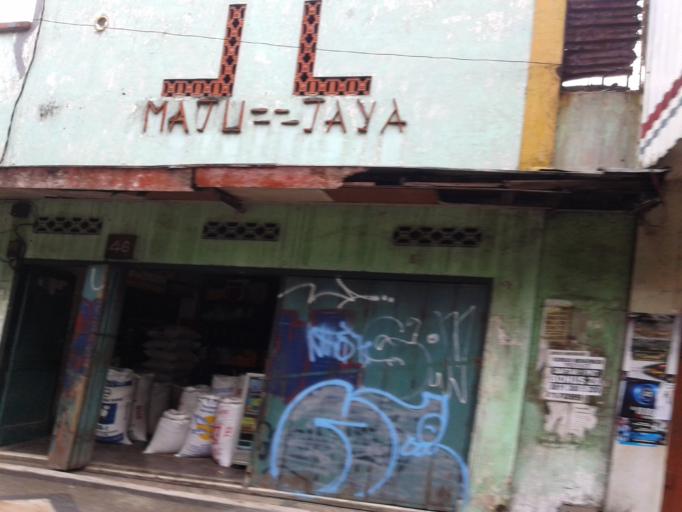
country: ID
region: East Java
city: Singosari
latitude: -7.8922
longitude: 112.6664
